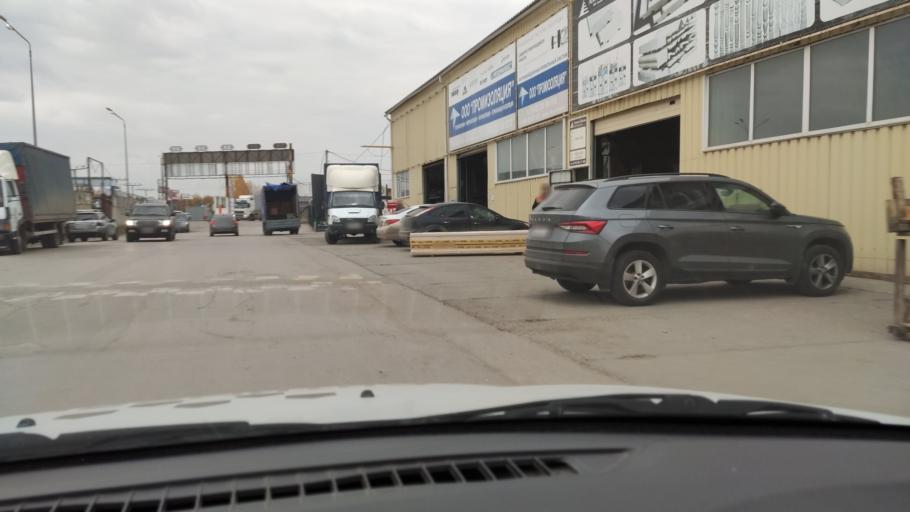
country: RU
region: Perm
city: Froly
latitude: 57.9576
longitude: 56.2769
